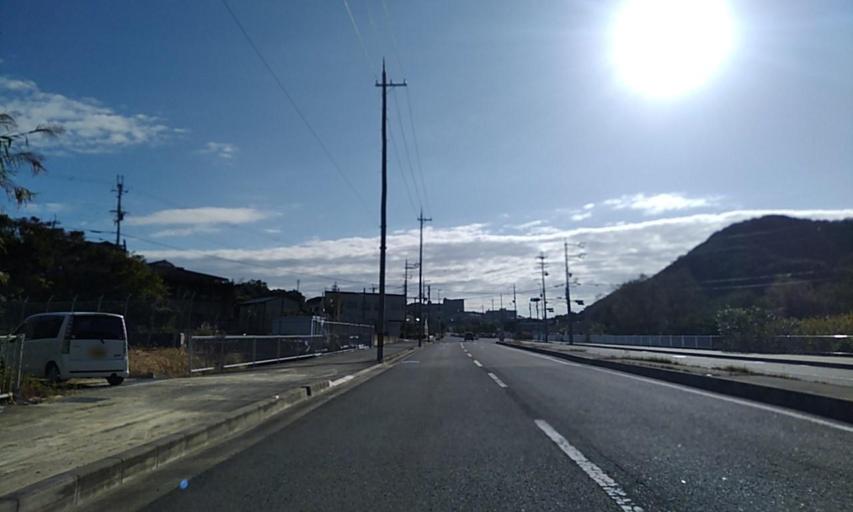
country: JP
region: Wakayama
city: Minato
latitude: 34.2691
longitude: 135.0885
